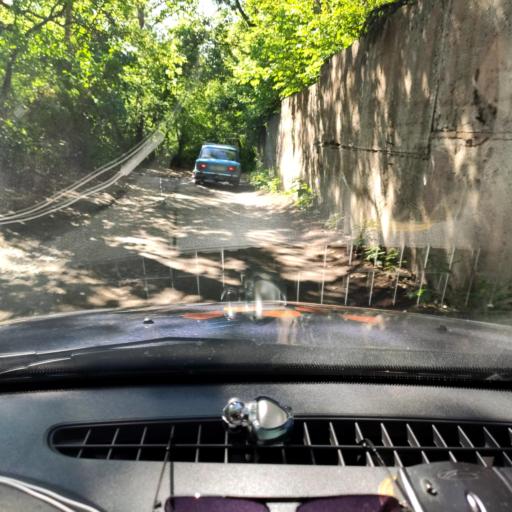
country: RU
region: Orjol
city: Orel
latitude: 52.9849
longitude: 36.0403
